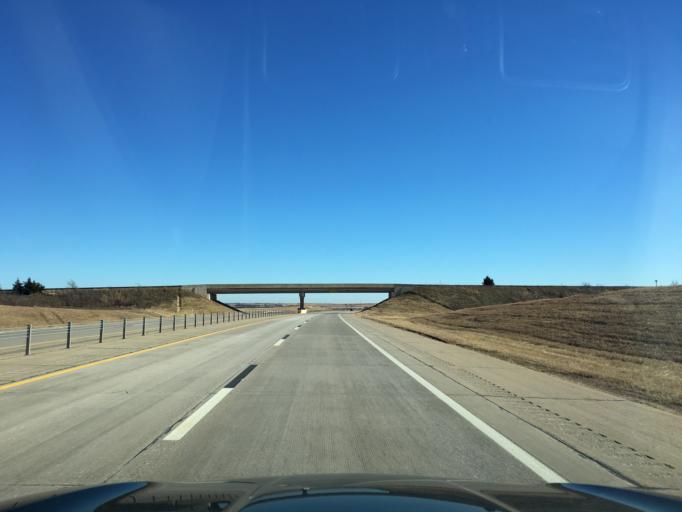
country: US
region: Oklahoma
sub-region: Noble County
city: Perry
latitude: 36.3917
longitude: -97.1055
